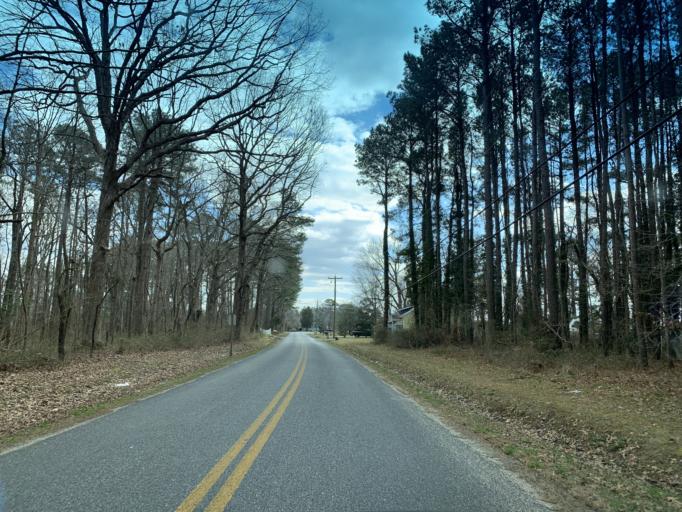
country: US
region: Maryland
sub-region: Queen Anne's County
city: Chester
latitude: 38.9419
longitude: -76.2825
